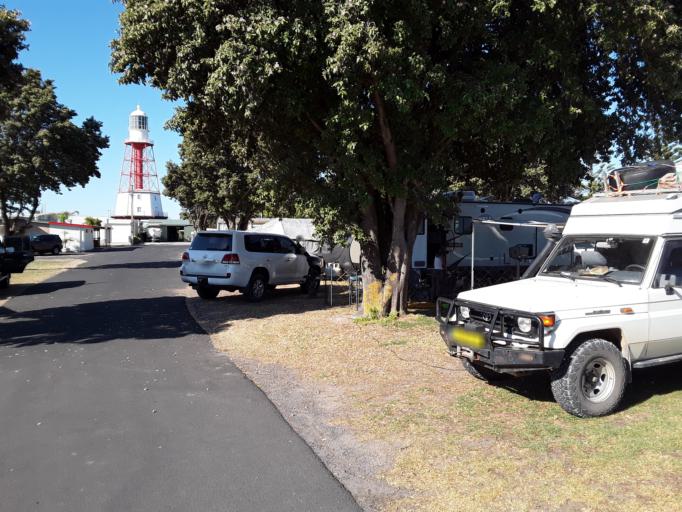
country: AU
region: South Australia
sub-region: Tatiara
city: Keith
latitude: -36.8372
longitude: 139.8456
